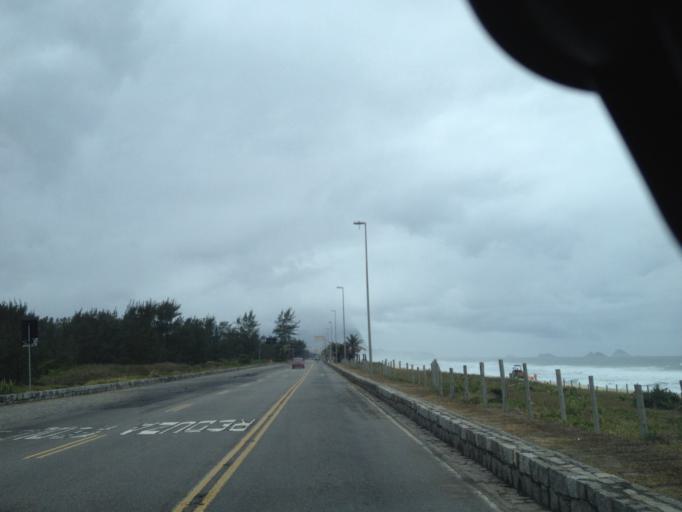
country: BR
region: Rio de Janeiro
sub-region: Nilopolis
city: Nilopolis
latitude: -23.0147
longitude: -43.4053
